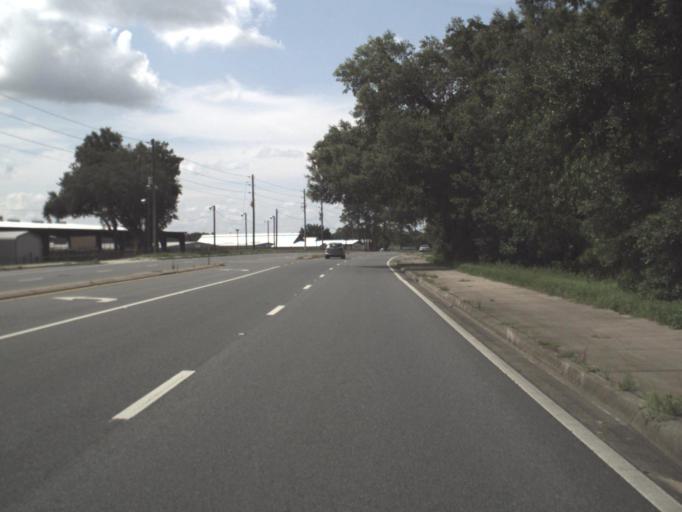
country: US
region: Florida
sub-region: Citrus County
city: Inverness Highlands South
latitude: 28.8069
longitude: -82.3125
